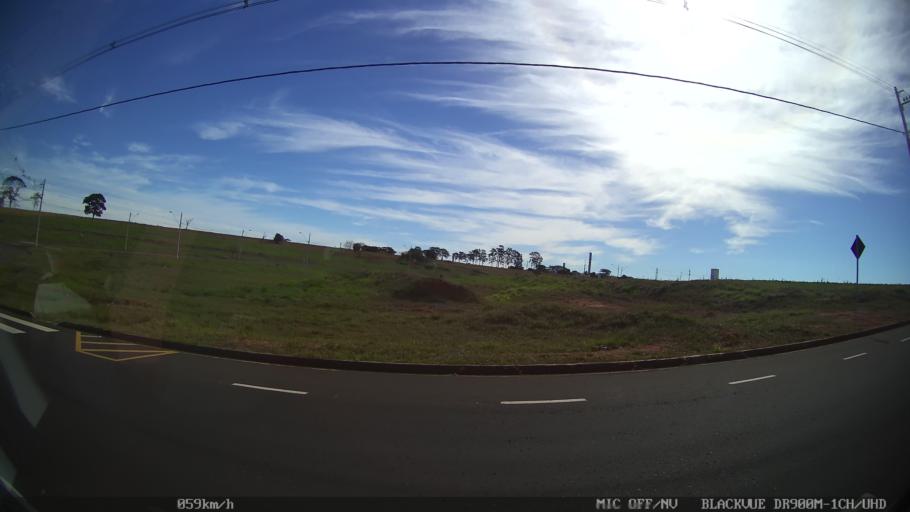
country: BR
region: Sao Paulo
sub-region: Sao Jose Do Rio Preto
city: Sao Jose do Rio Preto
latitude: -20.8545
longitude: -49.3778
